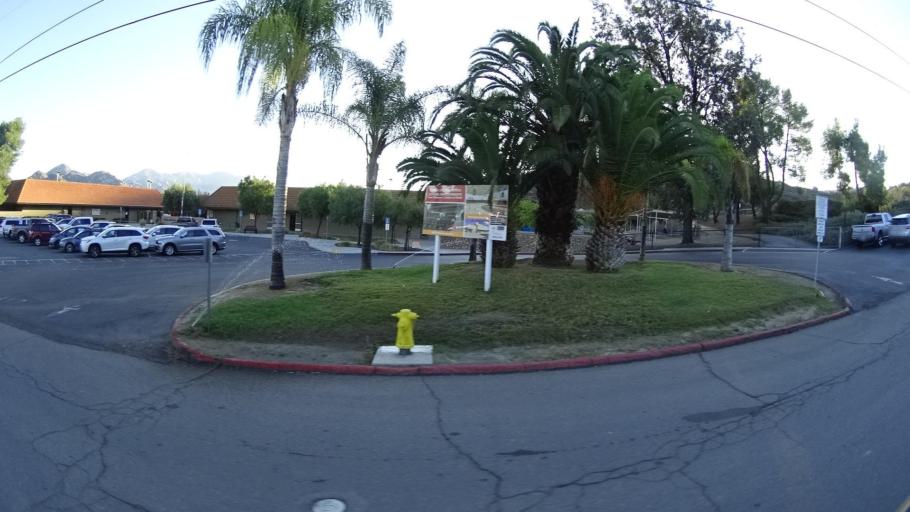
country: US
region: California
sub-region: San Diego County
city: Lakeside
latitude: 32.8532
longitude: -116.9115
